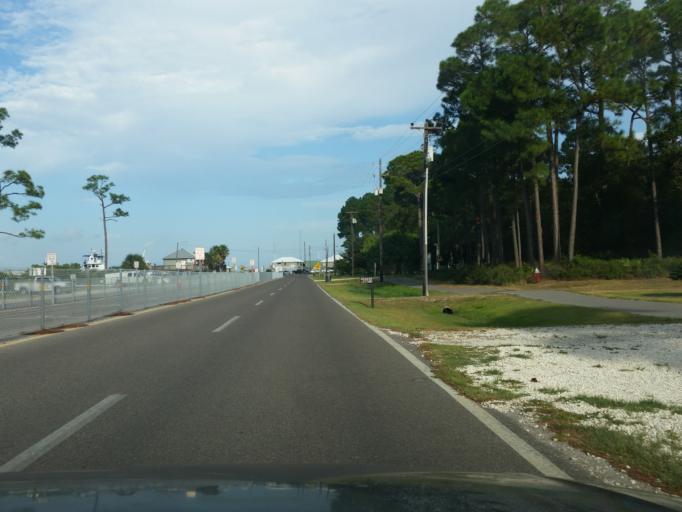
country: US
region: Alabama
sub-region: Mobile County
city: Dauphin Island
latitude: 30.2513
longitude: -88.0843
